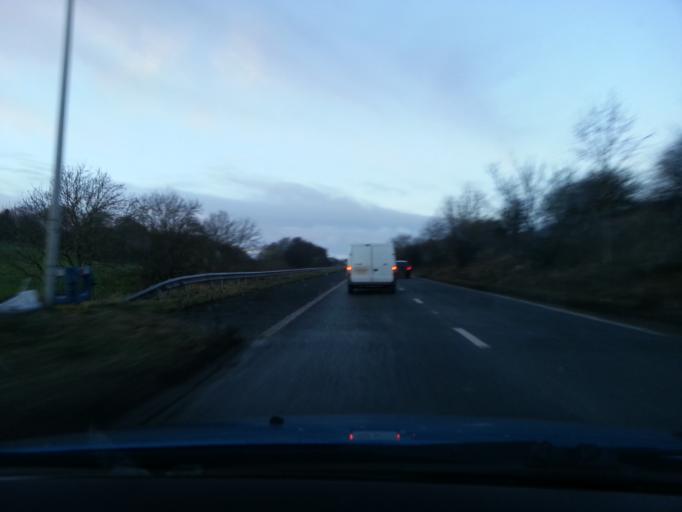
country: GB
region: England
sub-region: County Durham
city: Chester-le-Street
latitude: 54.8666
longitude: -1.5657
